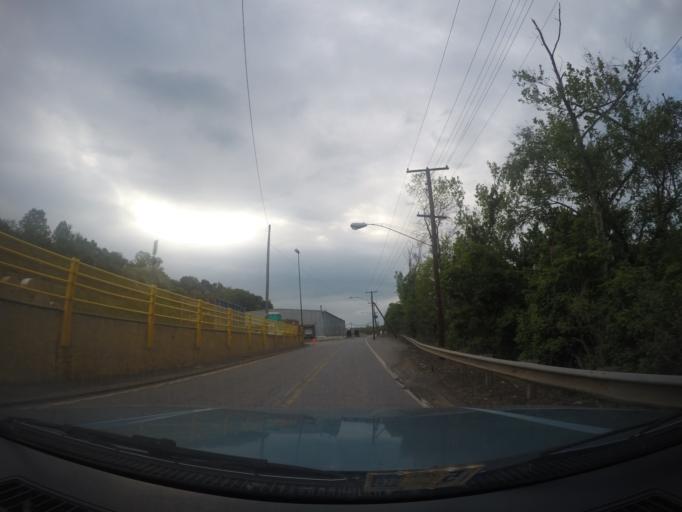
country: US
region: Virginia
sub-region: City of Lynchburg
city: Lynchburg
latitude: 37.4028
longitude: -79.1271
